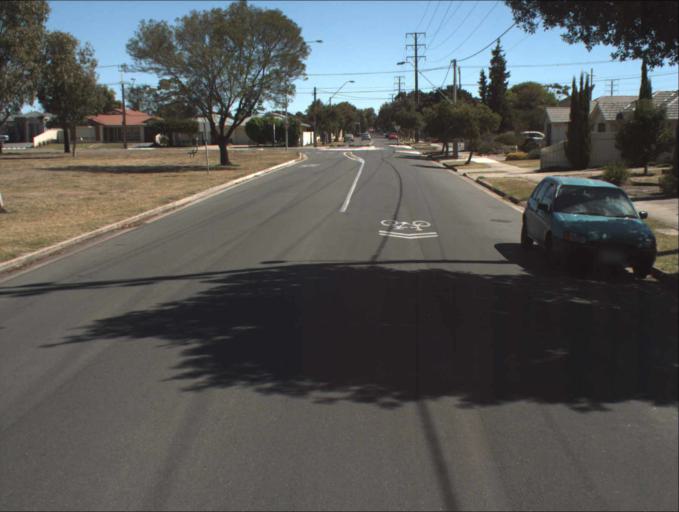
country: AU
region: South Australia
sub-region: Port Adelaide Enfield
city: Birkenhead
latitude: -34.8178
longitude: 138.4987
